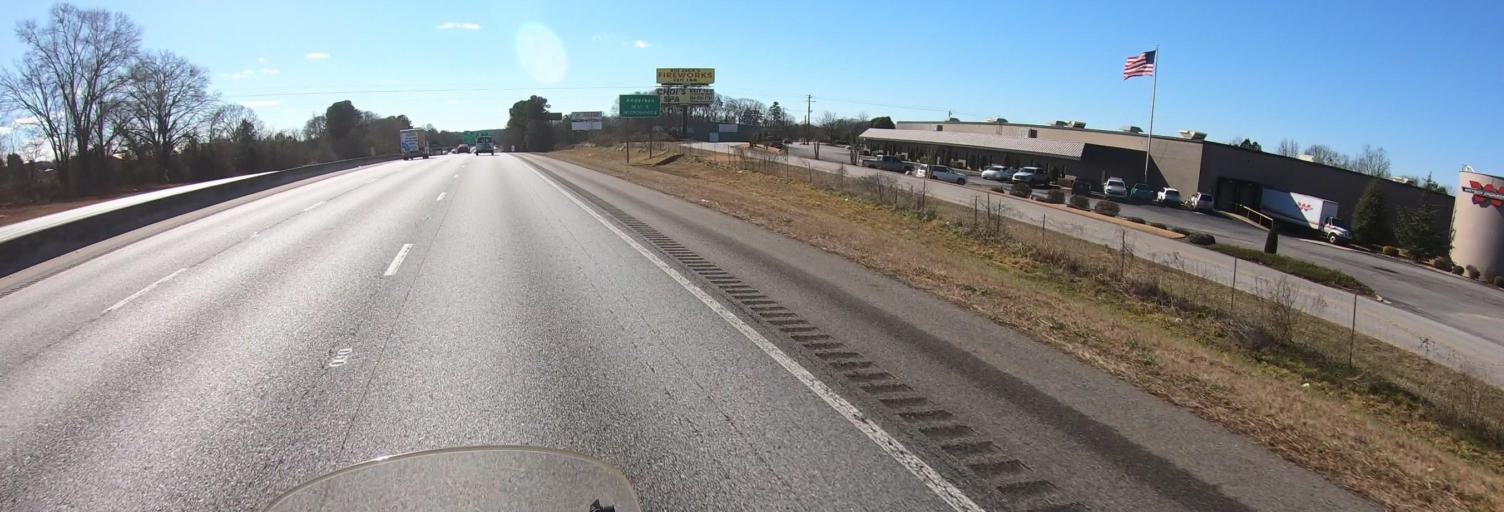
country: US
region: South Carolina
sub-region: Anderson County
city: Piedmont
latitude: 34.7039
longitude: -82.5021
